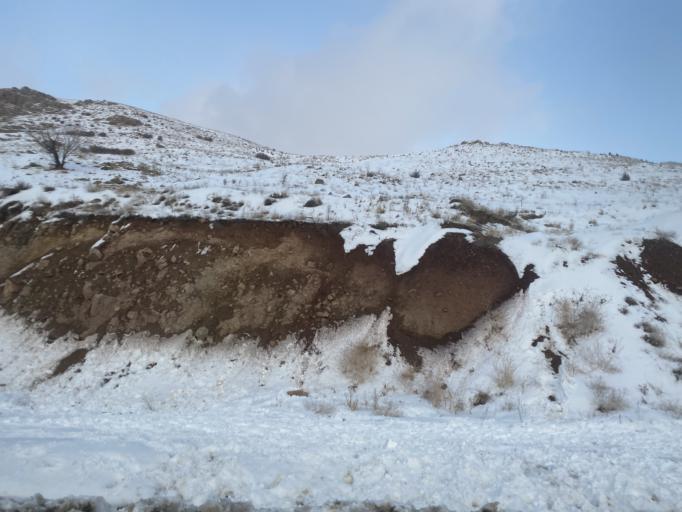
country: IR
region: Tehran
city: Damavand
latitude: 35.7834
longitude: 51.9552
